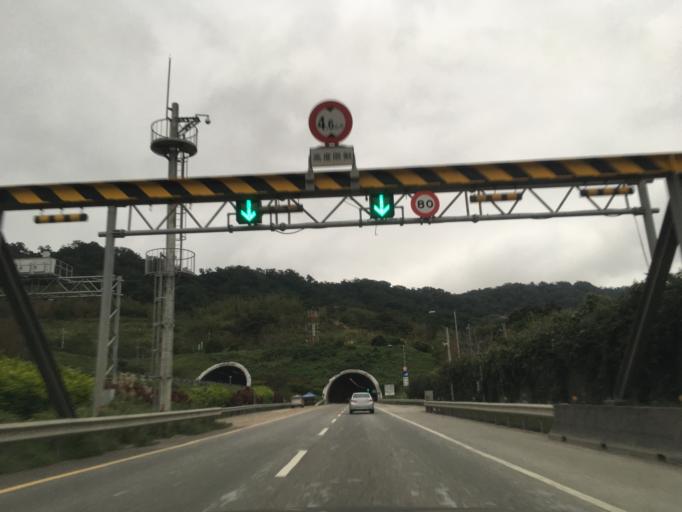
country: TW
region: Taipei
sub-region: Taipei
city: Banqiao
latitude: 25.1114
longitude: 121.4226
